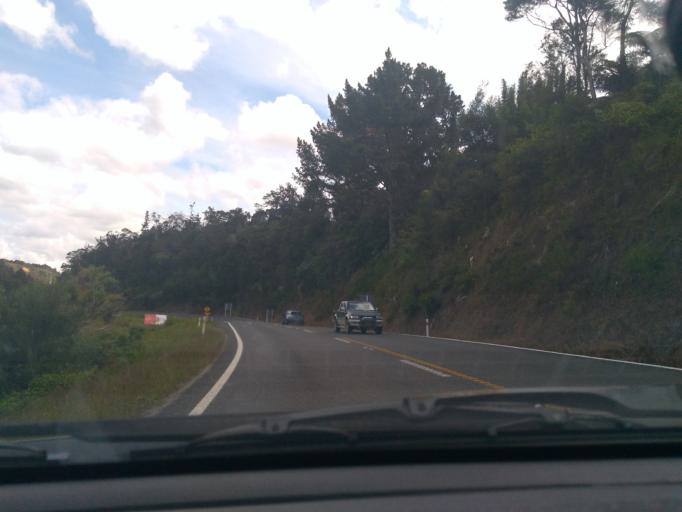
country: NZ
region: Northland
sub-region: Far North District
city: Kawakawa
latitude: -35.3820
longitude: 174.0712
